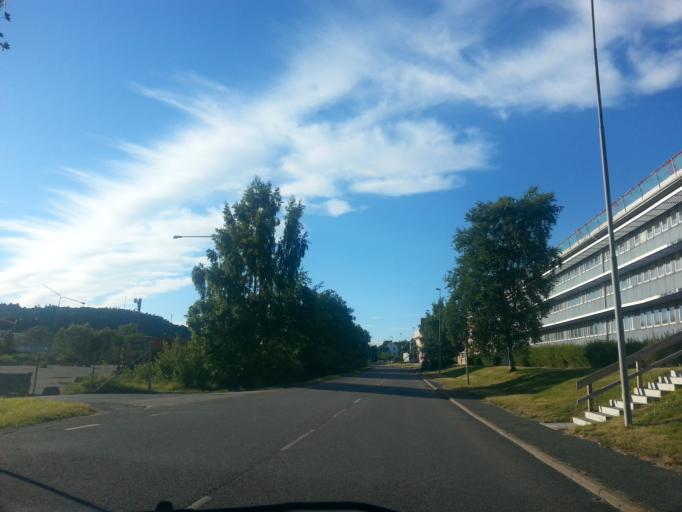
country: SE
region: Vaestra Goetaland
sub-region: Molndal
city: Moelndal
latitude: 57.6578
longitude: 12.0196
